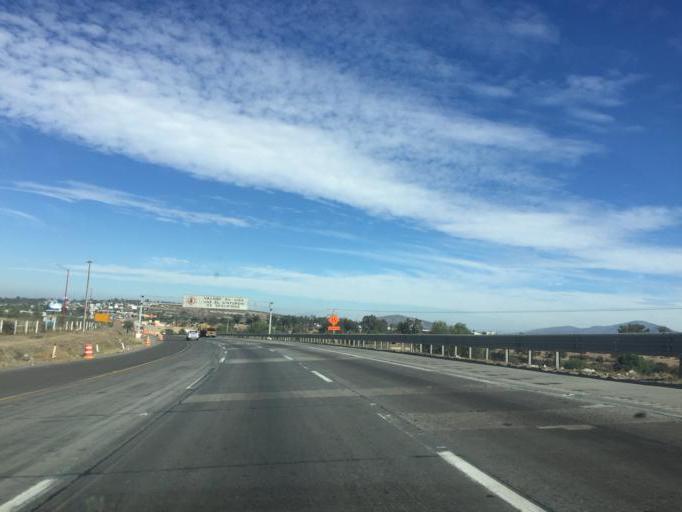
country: MX
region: Queretaro
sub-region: San Juan del Rio
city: Paso de Mata
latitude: 20.3161
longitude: -99.9309
